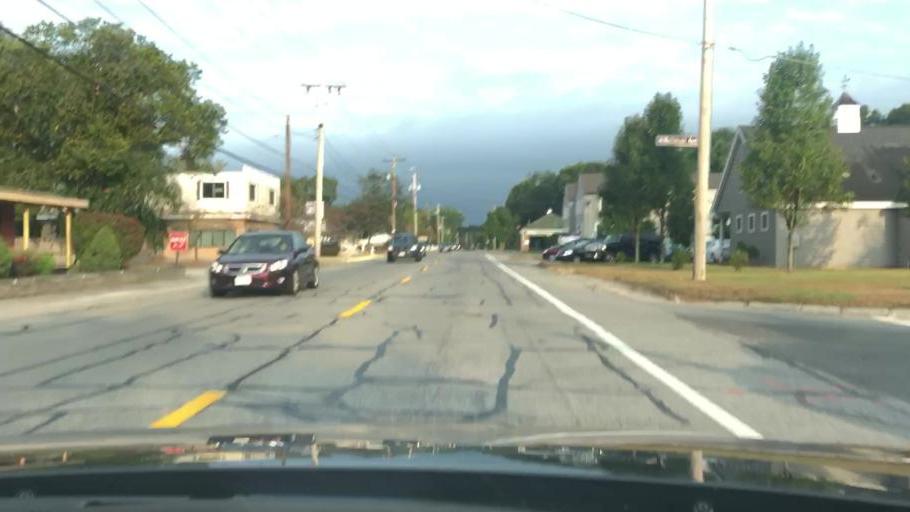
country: US
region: Massachusetts
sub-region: Middlesex County
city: Tyngsboro
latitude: 42.6445
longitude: -71.3913
